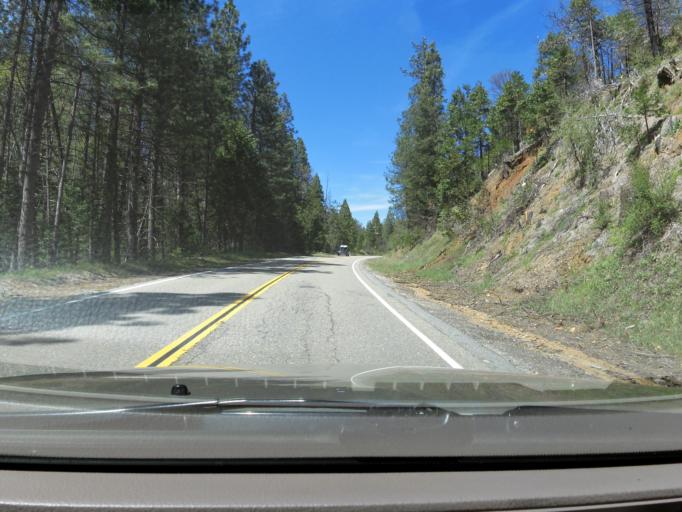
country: US
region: California
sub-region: Madera County
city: Oakhurst
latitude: 37.2826
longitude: -119.5766
